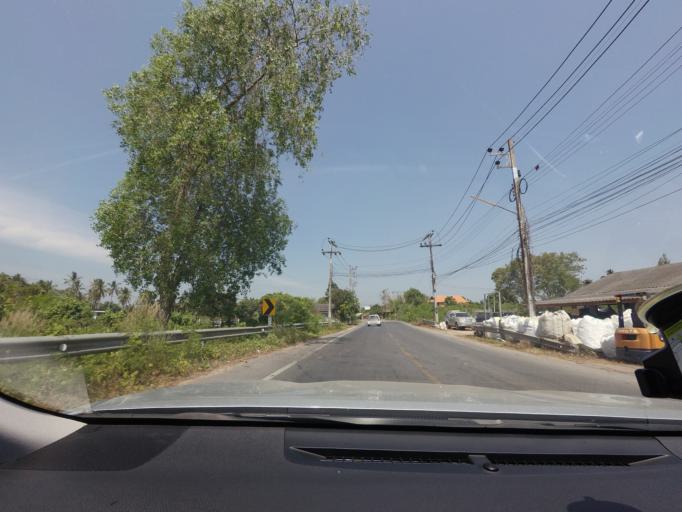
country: TH
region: Surat Thani
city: Phunphin
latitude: 9.1903
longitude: 99.2591
